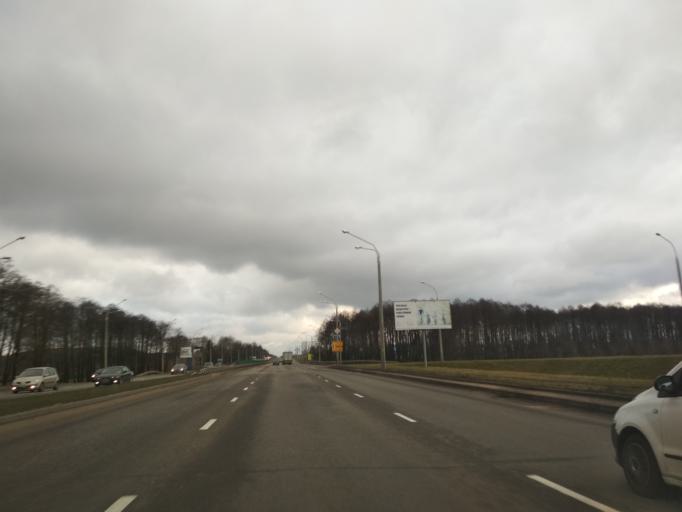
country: BY
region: Minsk
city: Vyaliki Trastsyanets
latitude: 53.8455
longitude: 27.7109
